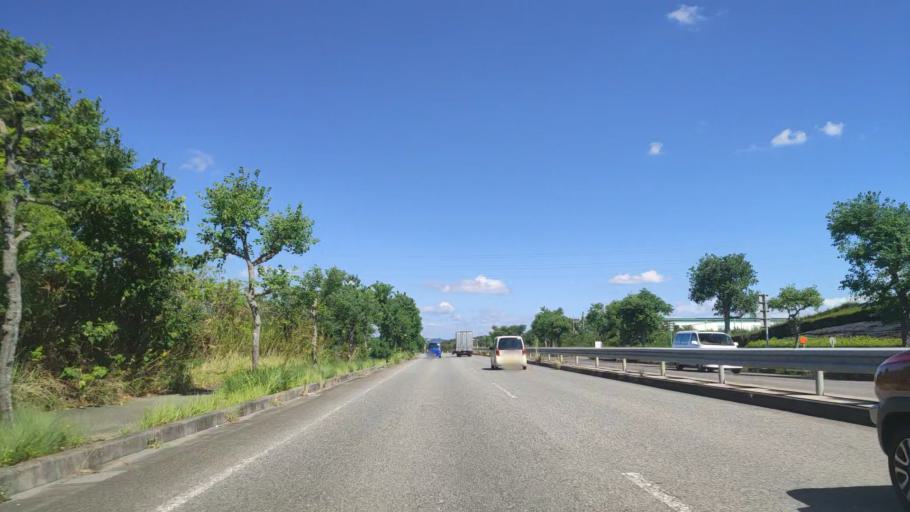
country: JP
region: Hyogo
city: Ono
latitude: 34.8697
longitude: 134.9522
